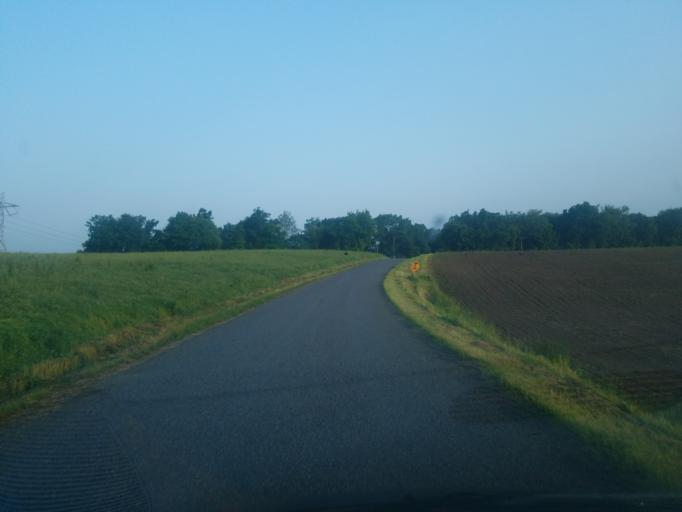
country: US
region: Ohio
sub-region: Stark County
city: Minerva
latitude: 40.7299
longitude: -81.0345
